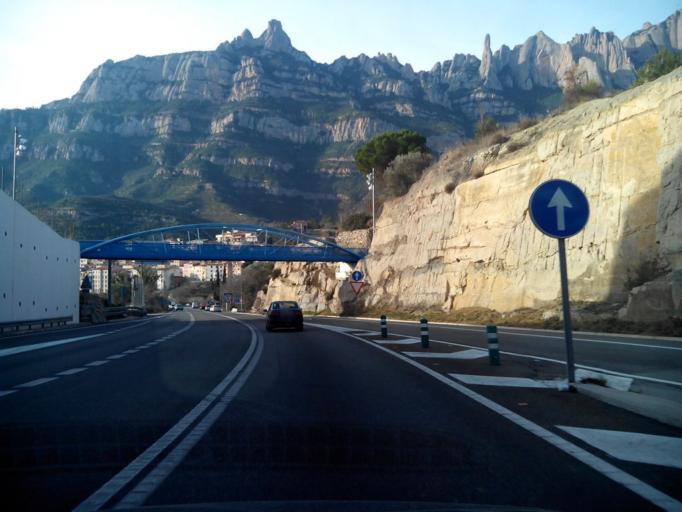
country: ES
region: Catalonia
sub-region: Provincia de Barcelona
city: Monistrol de Montserrat
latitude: 41.6161
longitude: 1.8457
